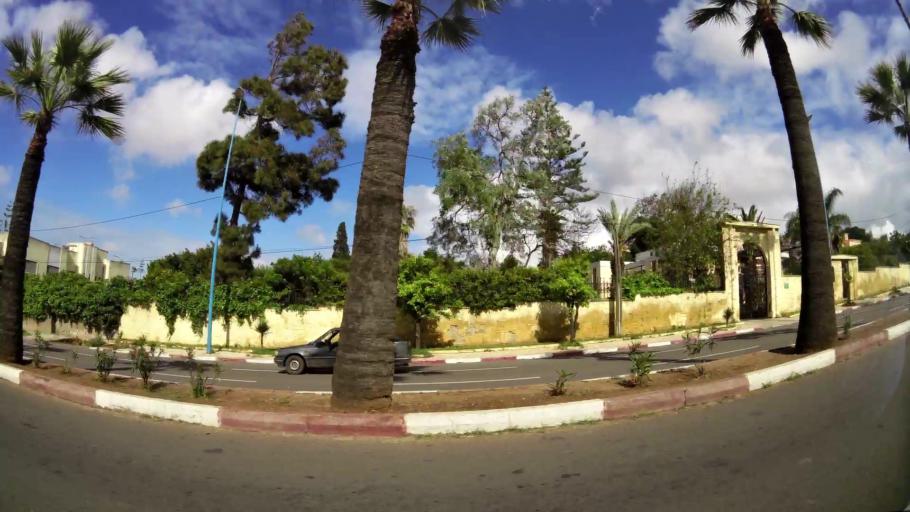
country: MA
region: Grand Casablanca
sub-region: Casablanca
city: Casablanca
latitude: 33.5507
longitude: -7.6230
